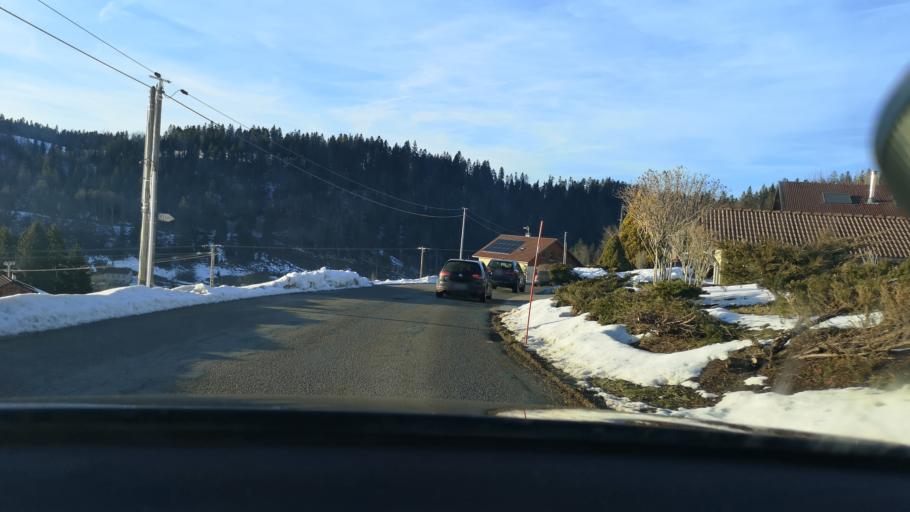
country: FR
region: Franche-Comte
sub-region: Departement du Doubs
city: Montlebon
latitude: 46.9937
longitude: 6.5504
